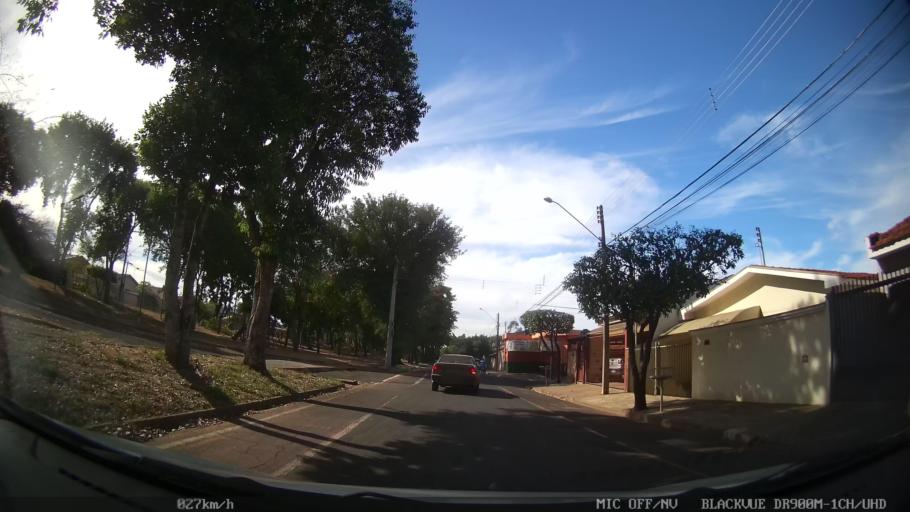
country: BR
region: Sao Paulo
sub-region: Catanduva
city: Catanduva
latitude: -21.1159
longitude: -48.9660
